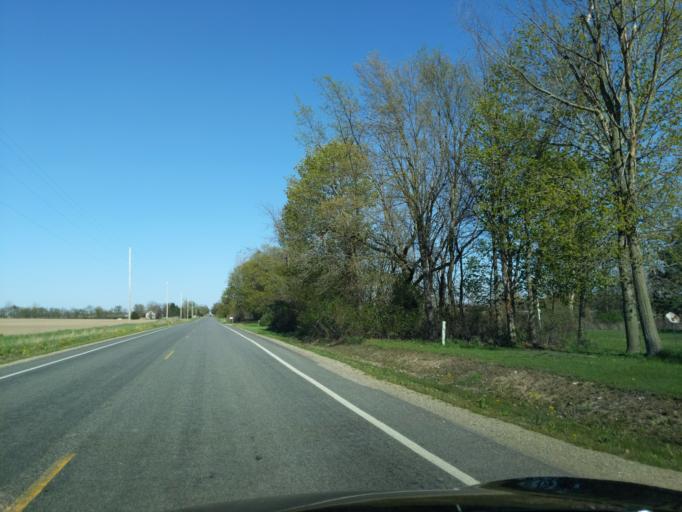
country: US
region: Michigan
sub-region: Ionia County
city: Ionia
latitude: 42.8861
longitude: -85.1007
